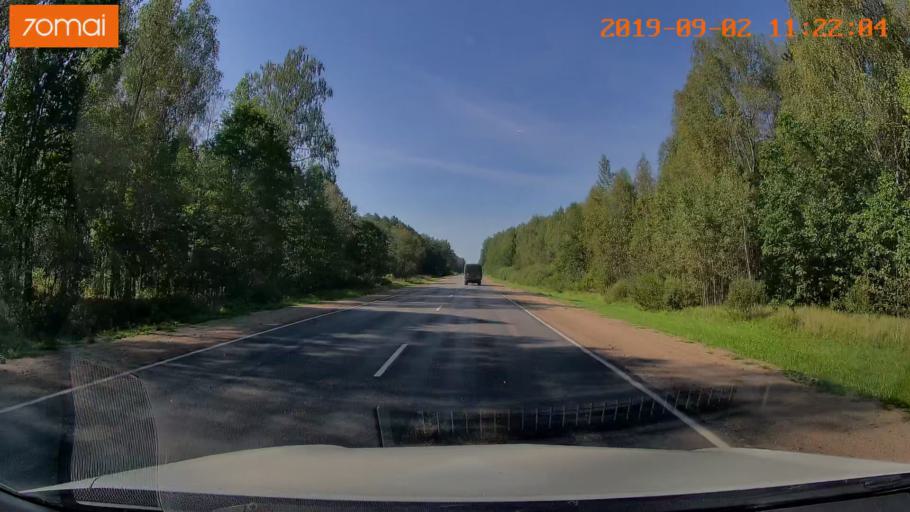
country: RU
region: Smolensk
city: Roslavl'
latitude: 54.0294
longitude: 33.0220
